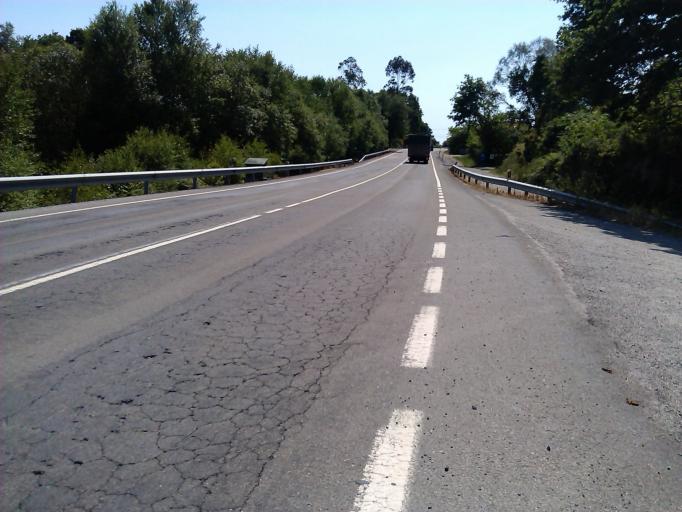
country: ES
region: Galicia
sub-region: Provincia de Lugo
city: Monterroso
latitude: 42.8721
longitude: -7.8823
